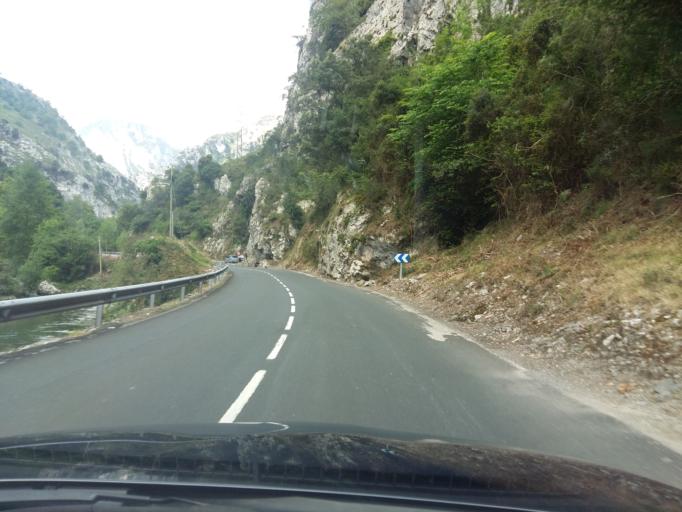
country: ES
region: Cantabria
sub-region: Provincia de Cantabria
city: Tresviso
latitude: 43.2943
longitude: -4.6113
